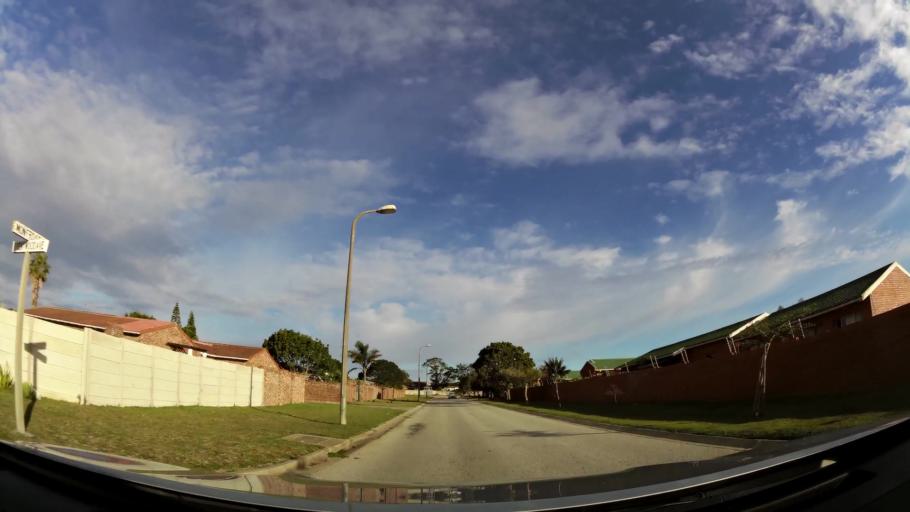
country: ZA
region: Eastern Cape
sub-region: Nelson Mandela Bay Metropolitan Municipality
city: Port Elizabeth
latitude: -33.9582
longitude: 25.4881
